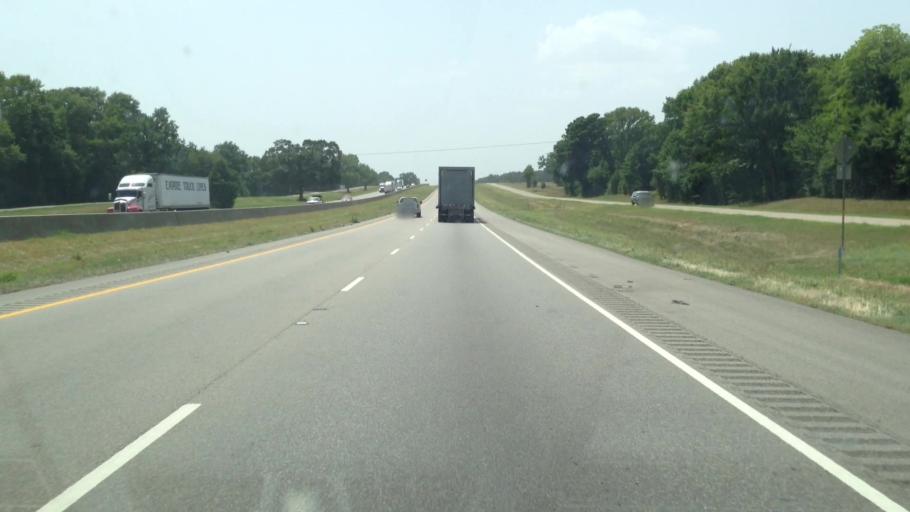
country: US
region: Texas
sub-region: Franklin County
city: Mount Vernon
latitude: 33.1614
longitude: -95.1366
